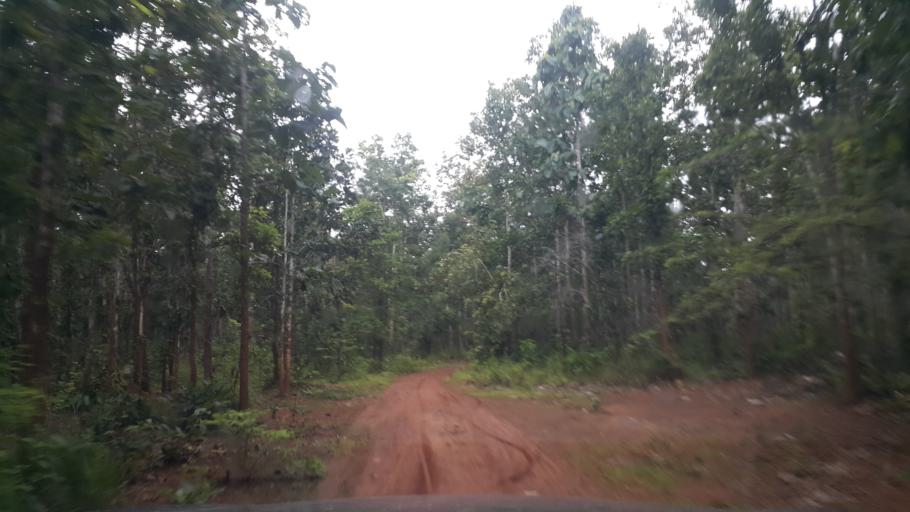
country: TH
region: Chiang Mai
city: San Sai
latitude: 18.9958
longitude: 99.1332
